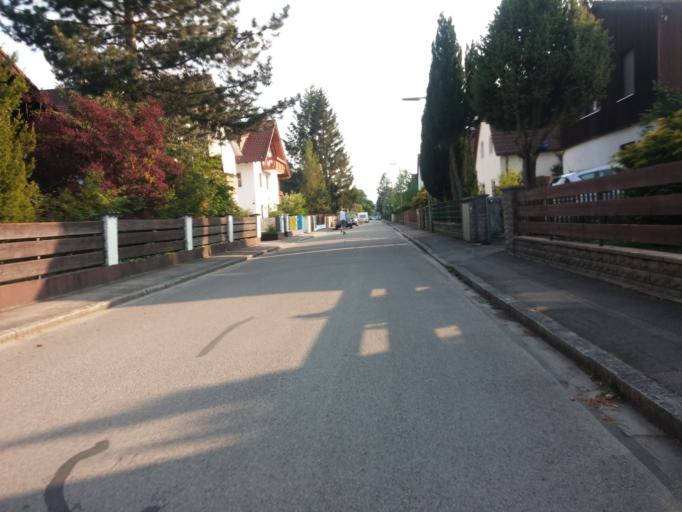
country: DE
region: Bavaria
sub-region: Upper Bavaria
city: Haar
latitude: 48.1326
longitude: 11.6755
